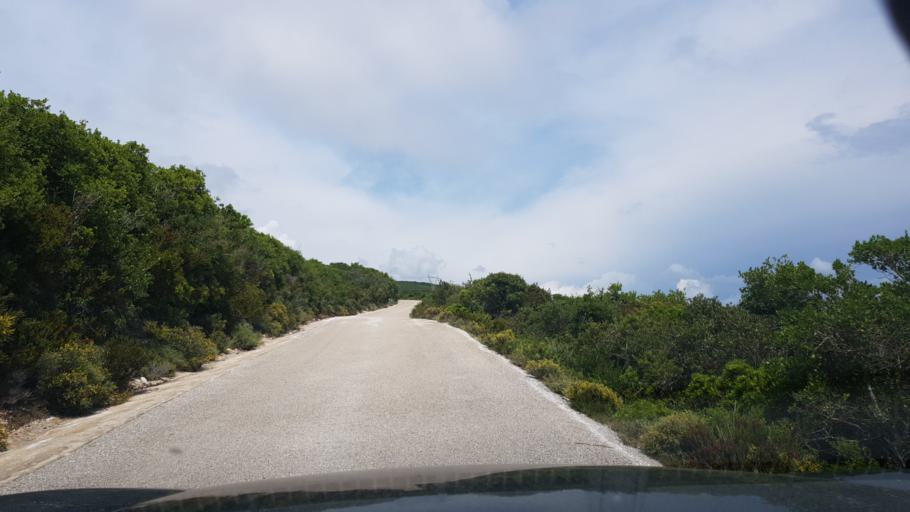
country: GR
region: Ionian Islands
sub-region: Lefkada
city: Nidri
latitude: 38.5958
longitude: 20.5535
